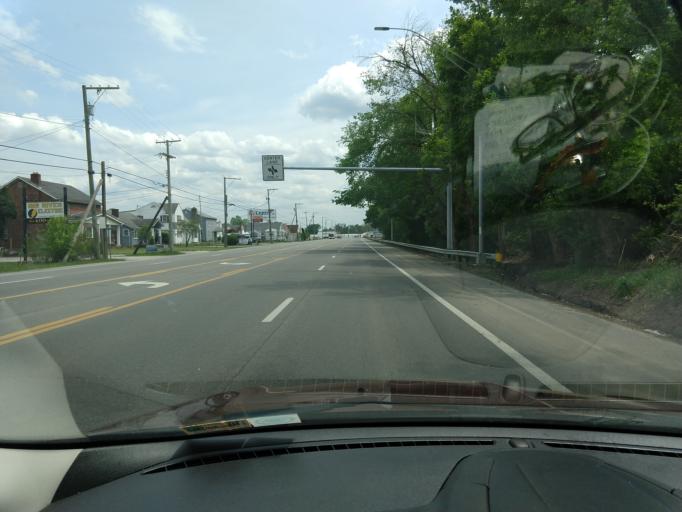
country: US
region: West Virginia
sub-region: Kanawha County
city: Dunbar
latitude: 38.3715
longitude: -81.7705
